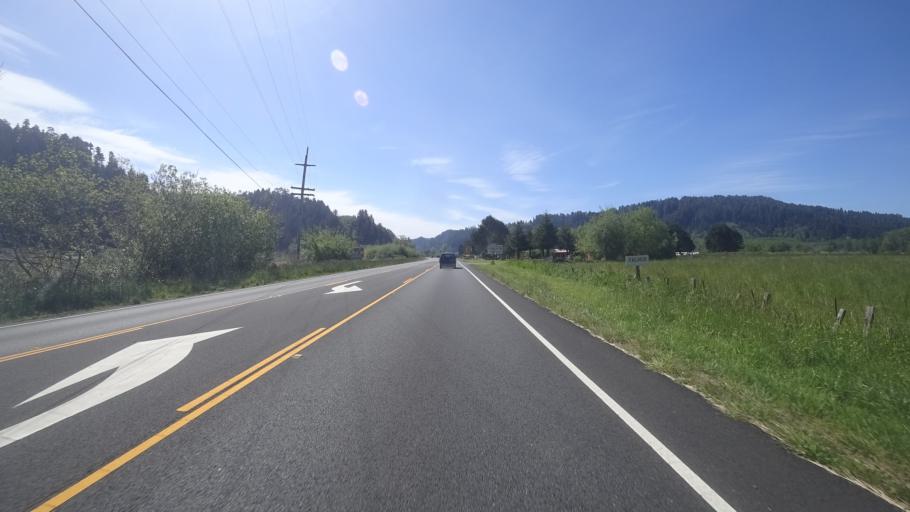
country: US
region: California
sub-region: Del Norte County
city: Bertsch-Oceanview
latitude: 41.5450
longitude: -124.0516
